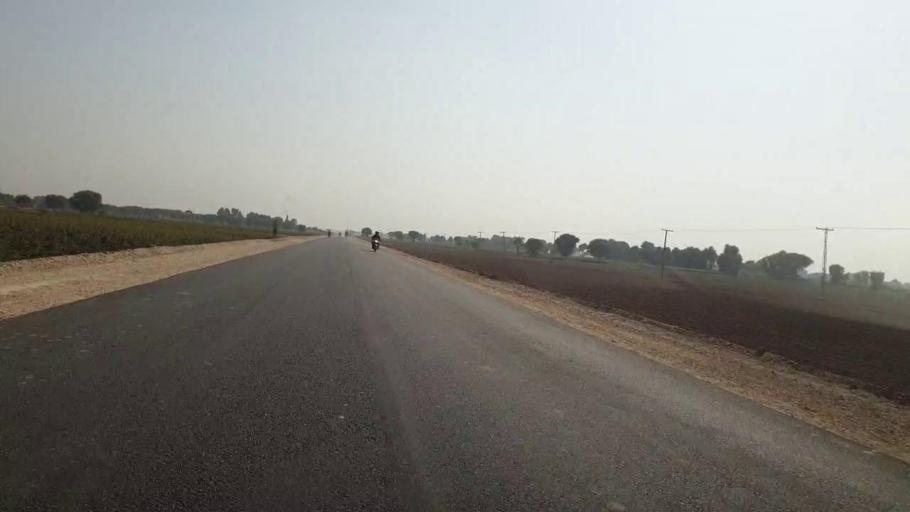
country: PK
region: Sindh
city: Dadu
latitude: 26.6669
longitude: 67.7765
